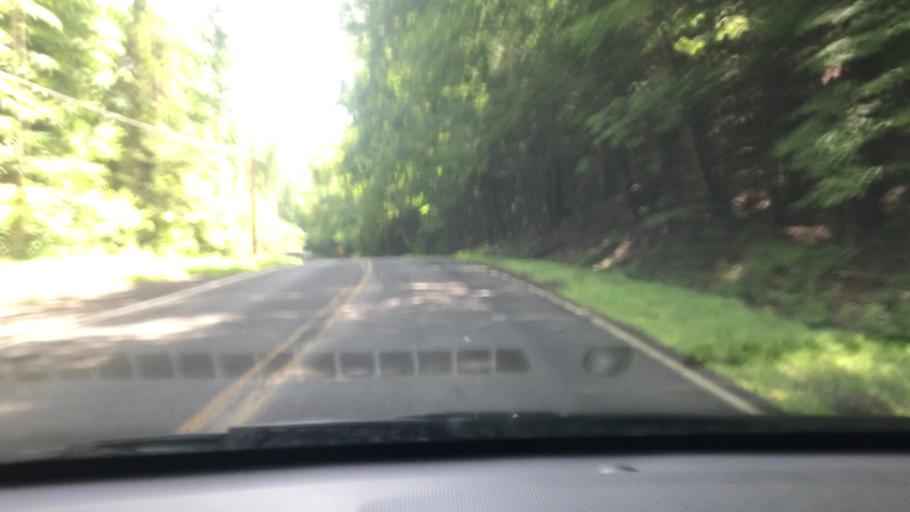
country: US
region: New York
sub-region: Ulster County
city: Stone Ridge
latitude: 41.8831
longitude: -74.1532
